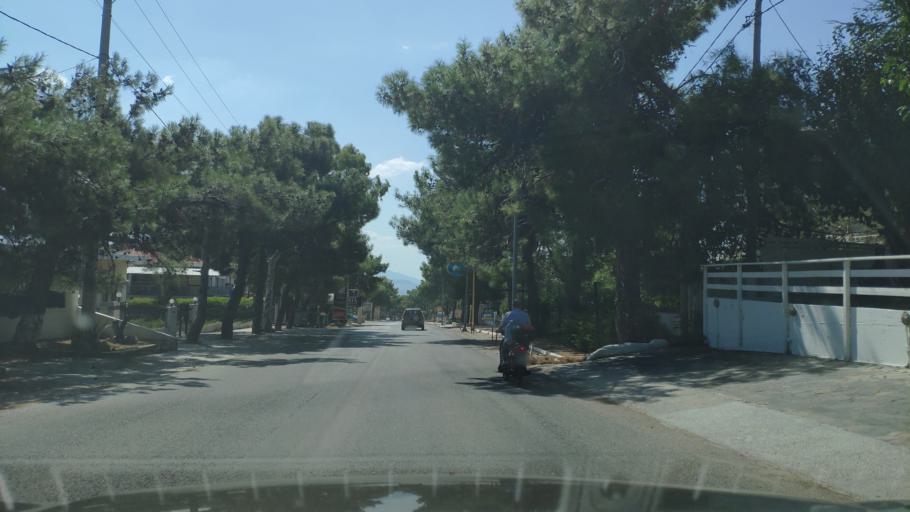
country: GR
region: Attica
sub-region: Nomarchia Anatolikis Attikis
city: Thrakomakedones
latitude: 38.1238
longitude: 23.7337
